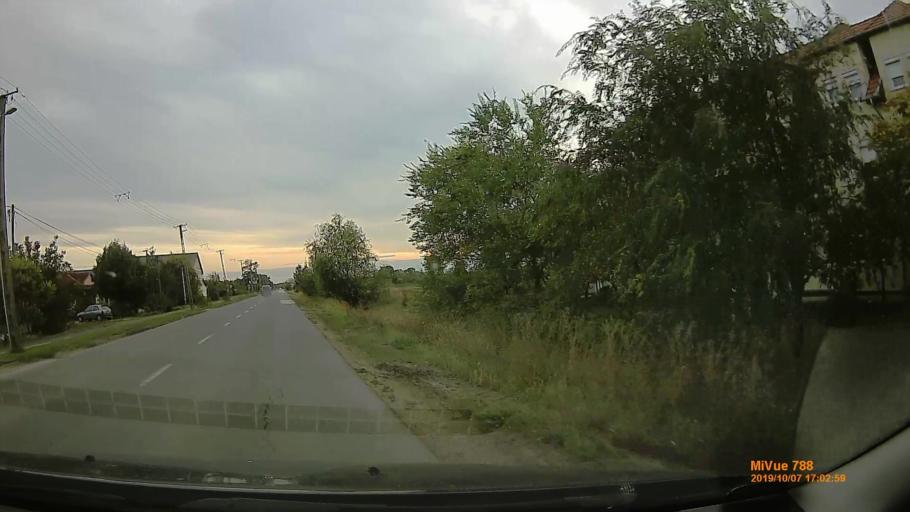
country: HU
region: Bekes
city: Szarvas
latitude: 46.8487
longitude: 20.5550
